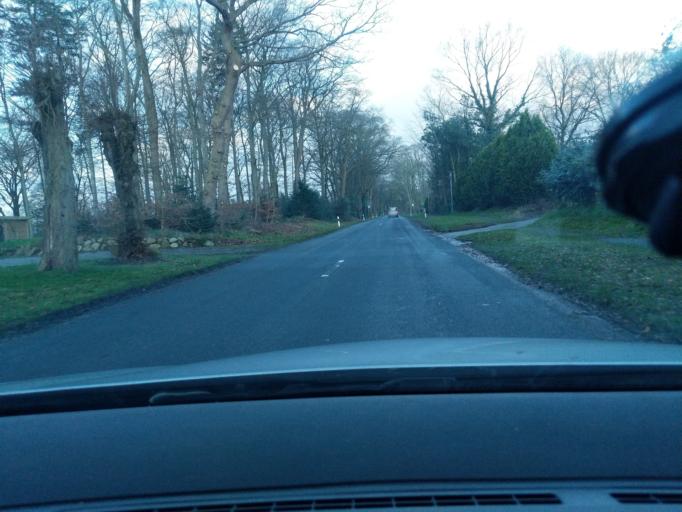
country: DE
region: Lower Saxony
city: Drangstedt
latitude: 53.6411
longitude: 8.7812
